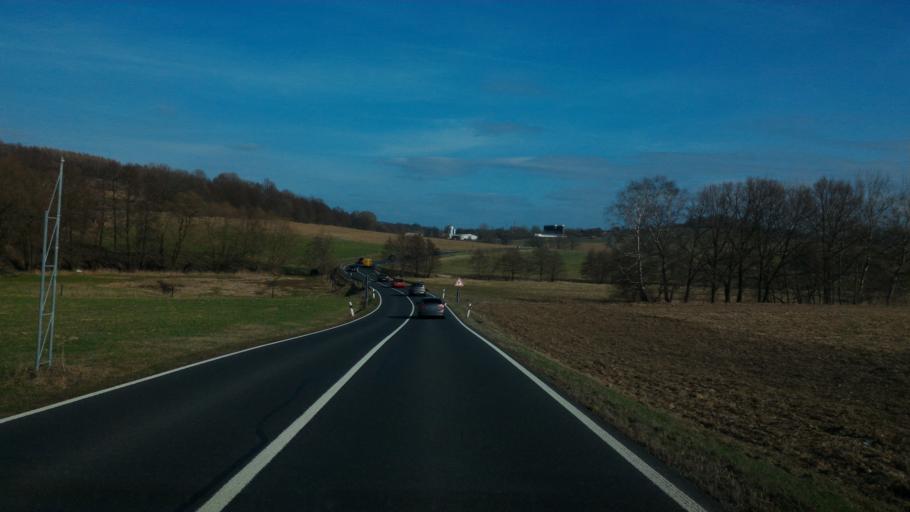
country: DE
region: Saxony
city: Neustadt in Sachsen
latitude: 51.0368
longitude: 14.1627
